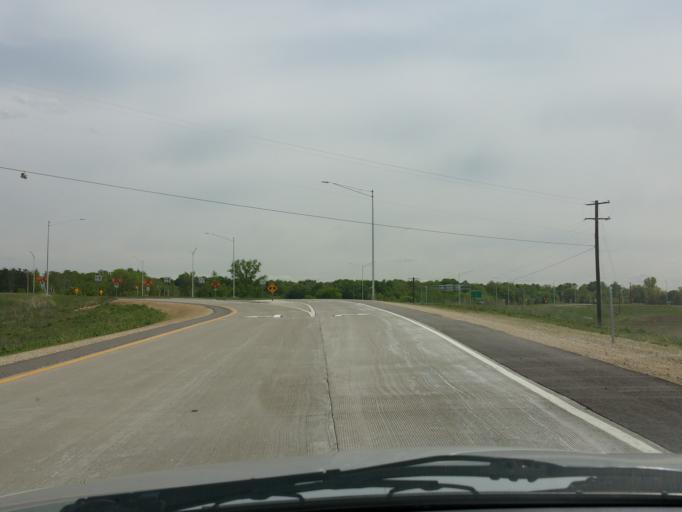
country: US
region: Wisconsin
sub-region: Pierce County
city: River Falls
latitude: 44.8985
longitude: -92.6505
